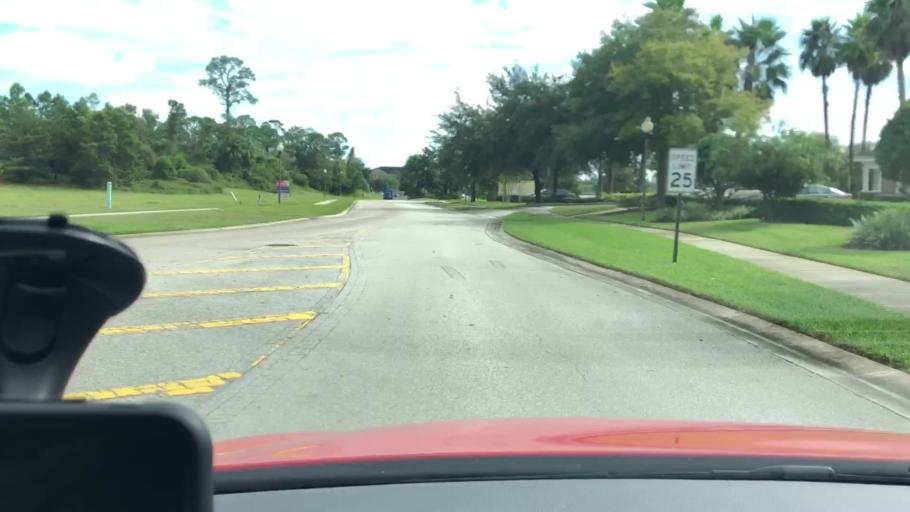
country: US
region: Florida
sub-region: Volusia County
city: South Daytona
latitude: 29.1523
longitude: -81.0350
